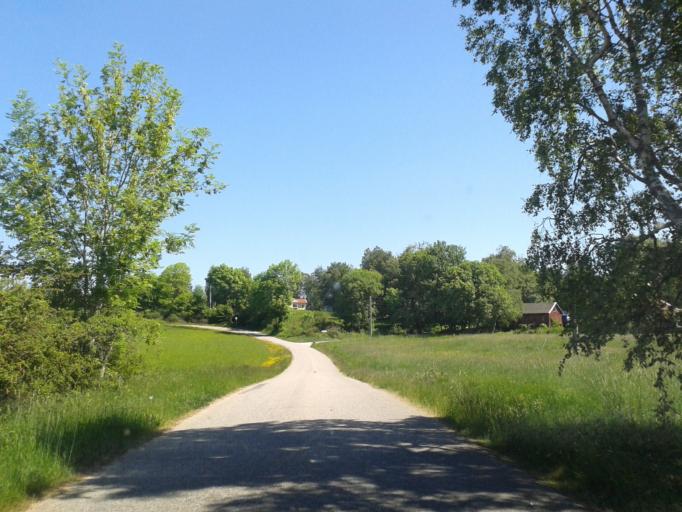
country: SE
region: Vaestra Goetaland
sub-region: Orust
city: Henan
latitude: 58.2740
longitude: 11.7590
